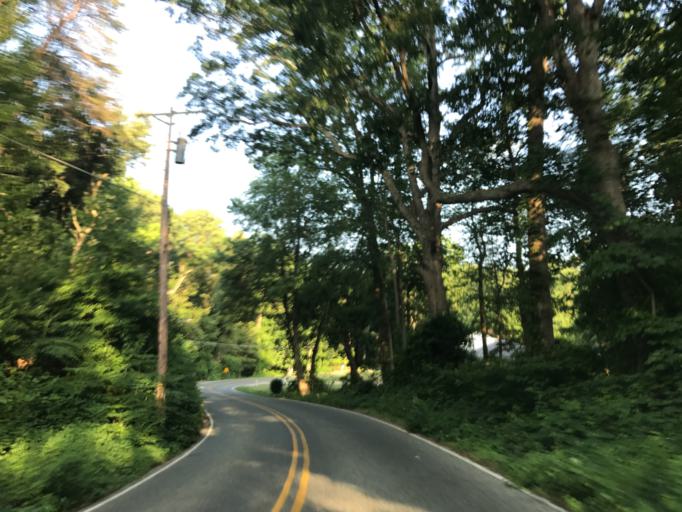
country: US
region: Maryland
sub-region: Harford County
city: Joppatowne
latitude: 39.4211
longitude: -76.3530
